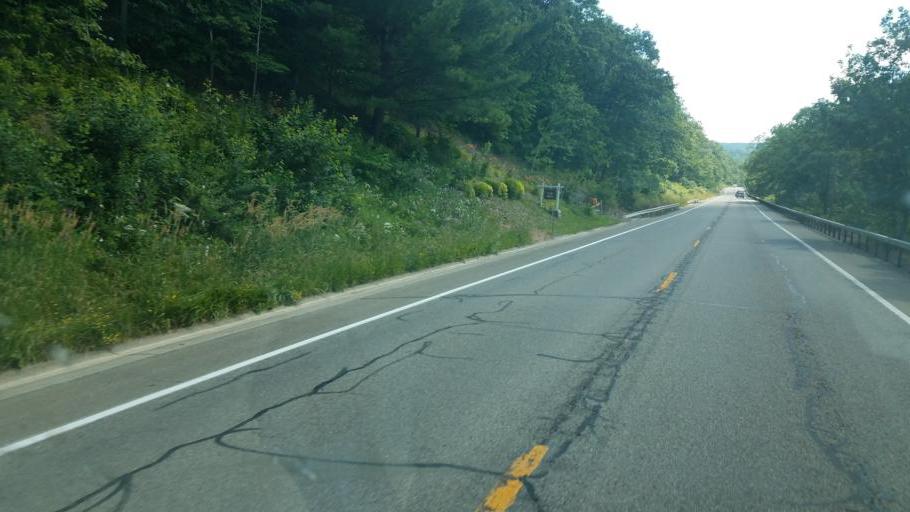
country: US
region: New York
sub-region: Steuben County
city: Sylvan Beach
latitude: 42.4097
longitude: -77.1989
